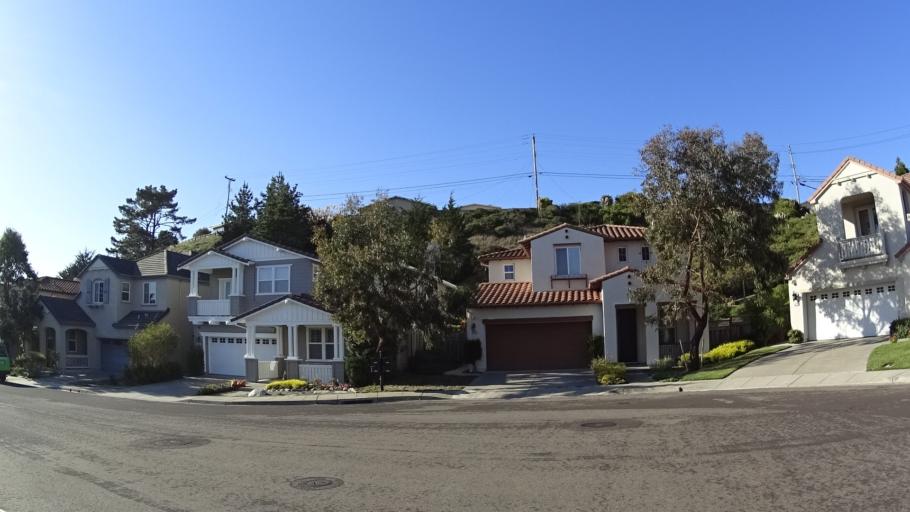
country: US
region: California
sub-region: San Mateo County
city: Pacifica
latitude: 37.6335
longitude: -122.4628
